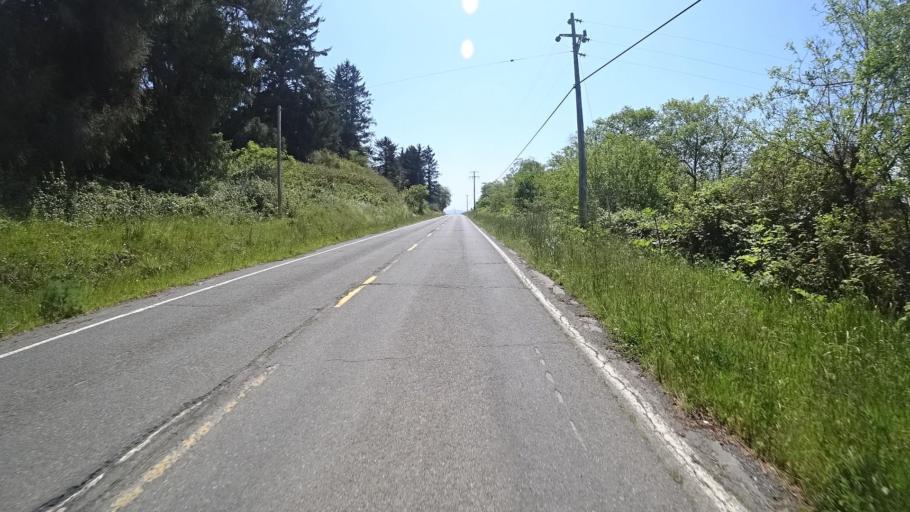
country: US
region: California
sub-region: Humboldt County
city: Ferndale
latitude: 40.6320
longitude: -124.2222
